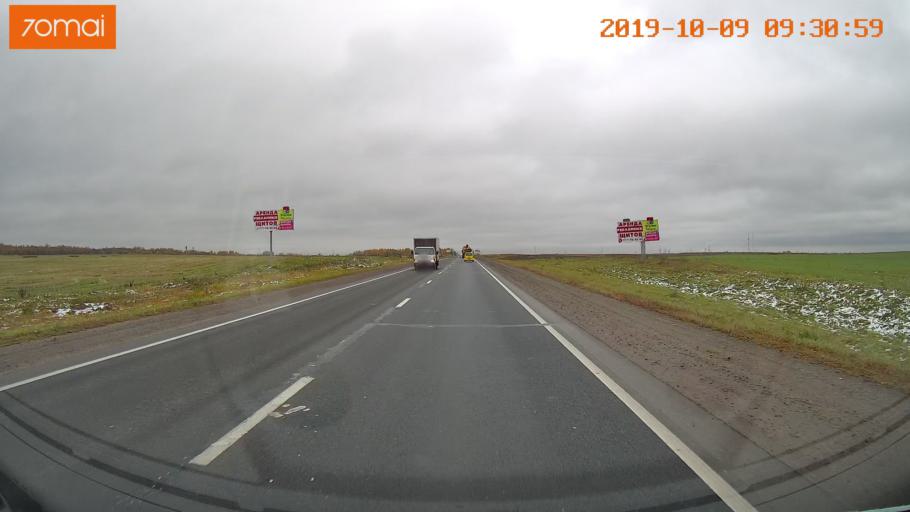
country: RU
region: Vologda
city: Vologda
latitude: 59.1452
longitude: 39.9434
